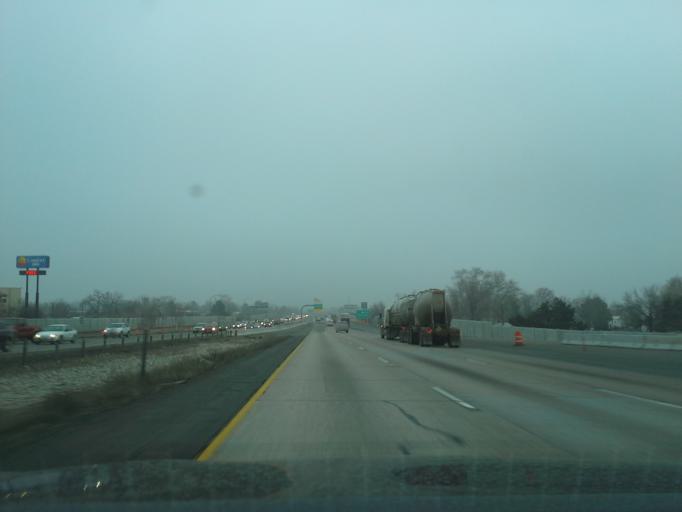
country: US
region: Utah
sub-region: Davis County
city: Layton
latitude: 41.0733
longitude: -111.9762
